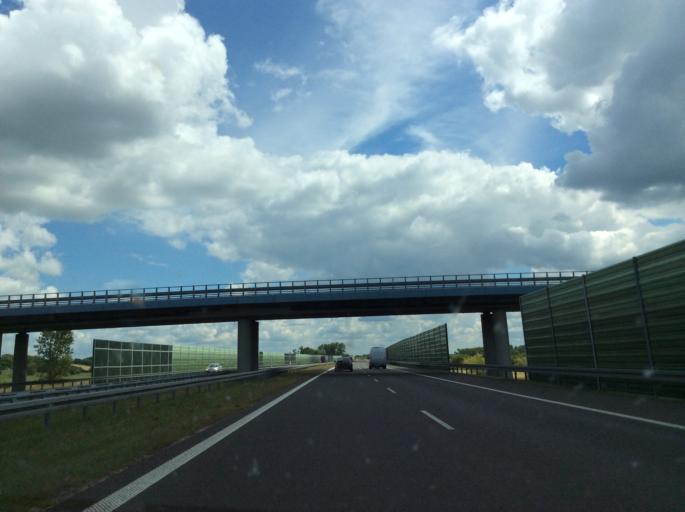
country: PL
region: Greater Poland Voivodeship
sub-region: Powiat kolski
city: Dabie
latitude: 52.1127
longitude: 18.7376
